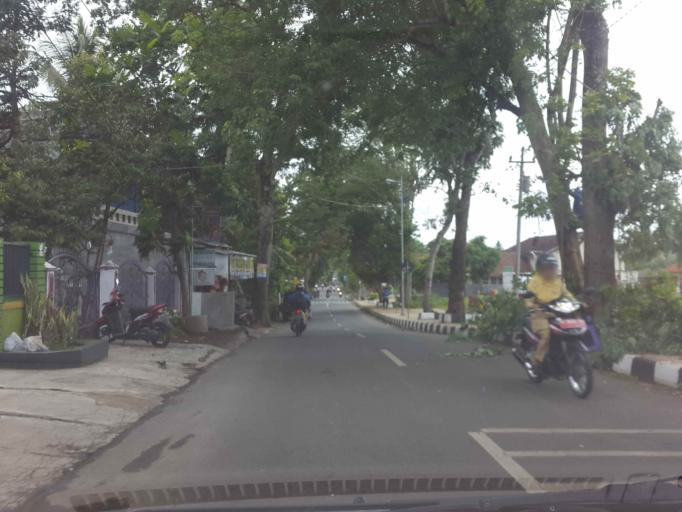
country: ID
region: Central Java
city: Salatiga
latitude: -7.3371
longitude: 110.5171
